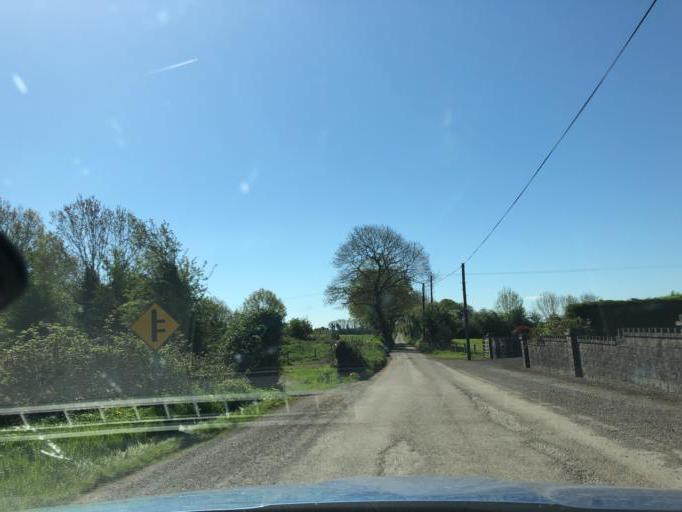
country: IE
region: Connaught
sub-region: County Galway
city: Portumna
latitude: 53.1485
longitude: -8.3395
